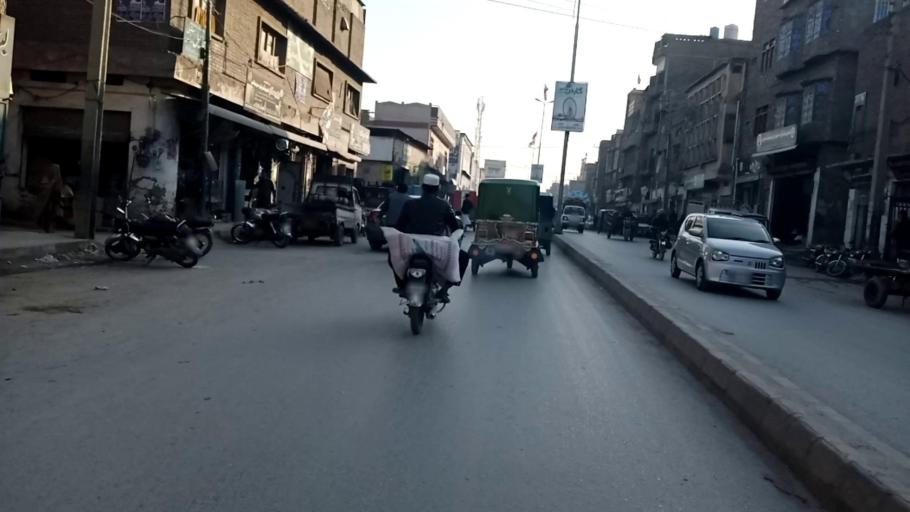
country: PK
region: Khyber Pakhtunkhwa
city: Peshawar
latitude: 34.0080
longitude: 71.5849
